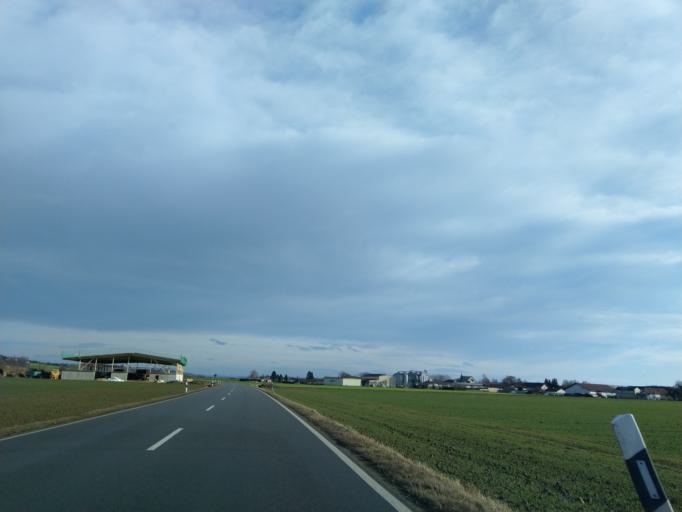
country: DE
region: Bavaria
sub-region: Lower Bavaria
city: Aldersbach
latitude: 48.6120
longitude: 13.0360
